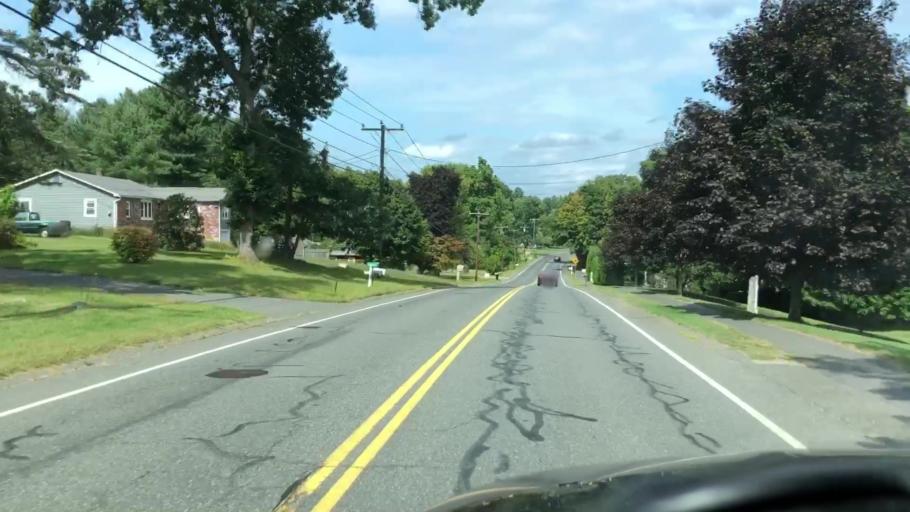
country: US
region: Massachusetts
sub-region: Hampshire County
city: Southampton
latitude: 42.2513
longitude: -72.7214
